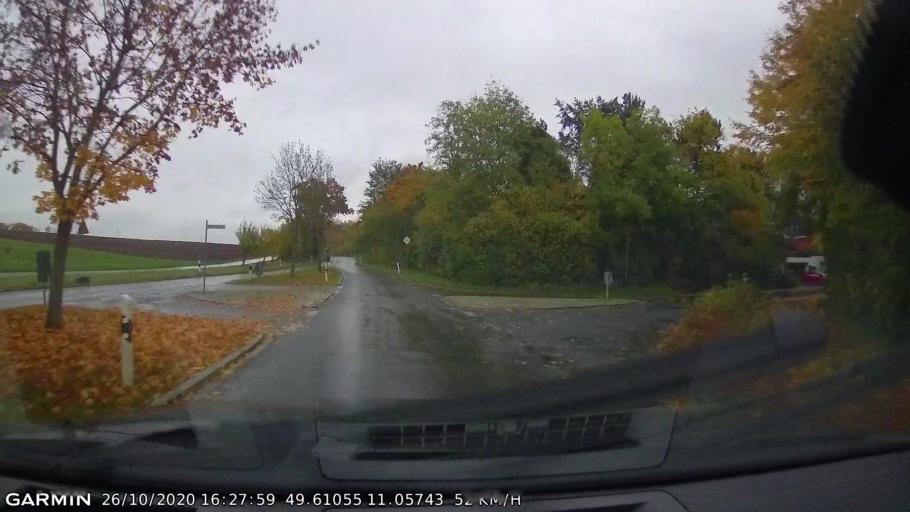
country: DE
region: Bavaria
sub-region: Regierungsbezirk Mittelfranken
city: Spardorf
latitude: 49.6107
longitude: 11.0577
